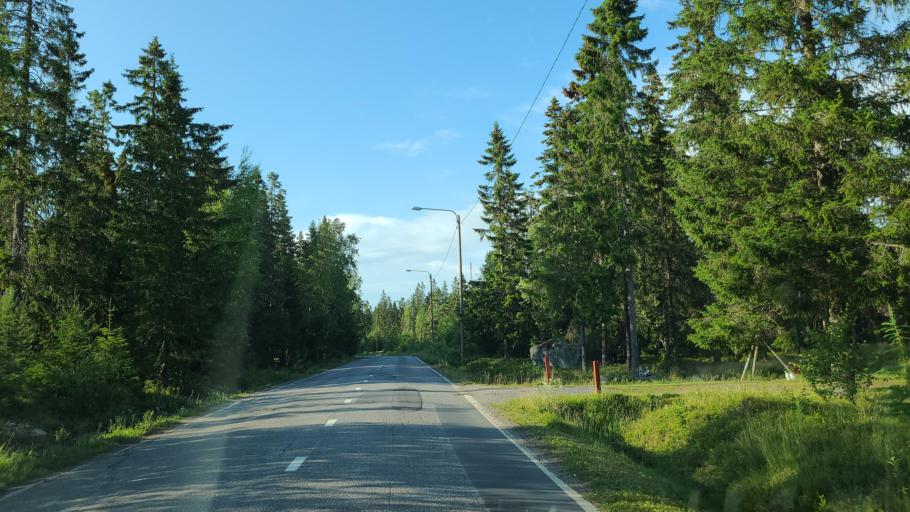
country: FI
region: Ostrobothnia
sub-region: Vaasa
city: Replot
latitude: 63.3551
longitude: 21.3032
